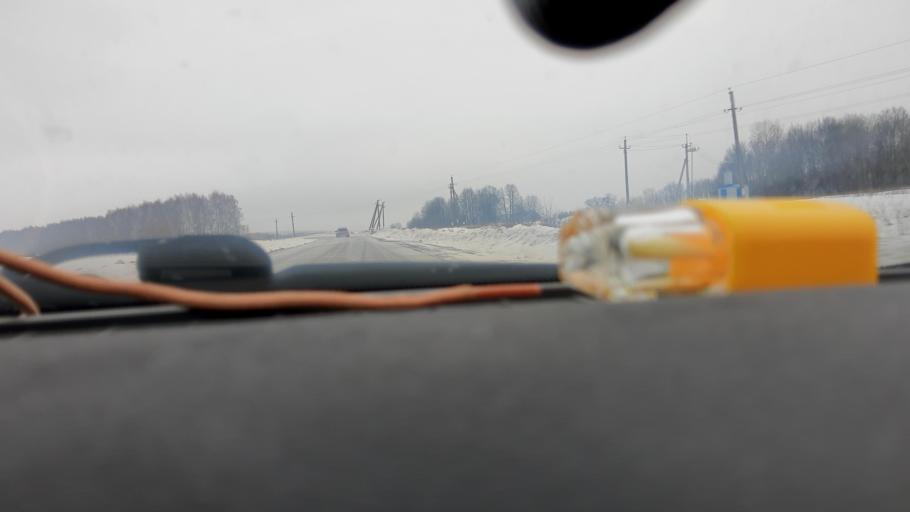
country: RU
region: Bashkortostan
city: Ulukulevo
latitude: 54.5868
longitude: 56.4252
